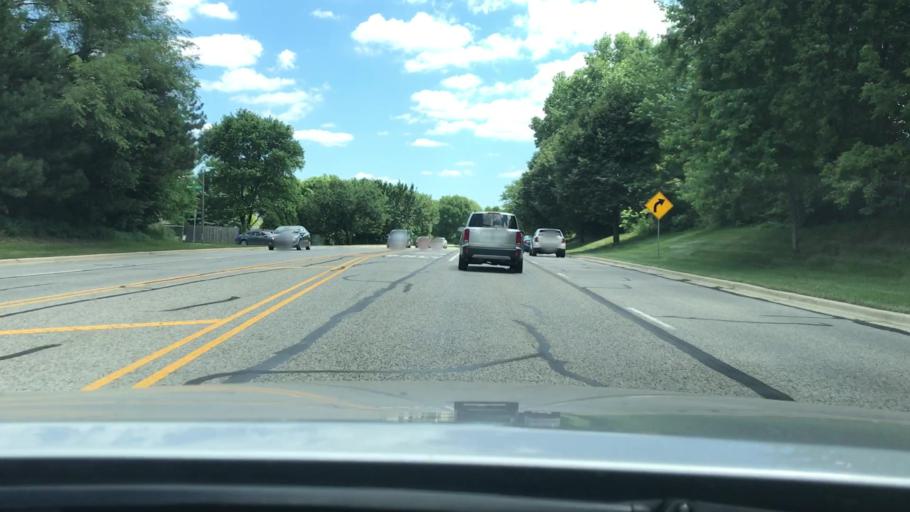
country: US
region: Illinois
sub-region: DuPage County
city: Naperville
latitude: 41.7853
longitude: -88.1129
